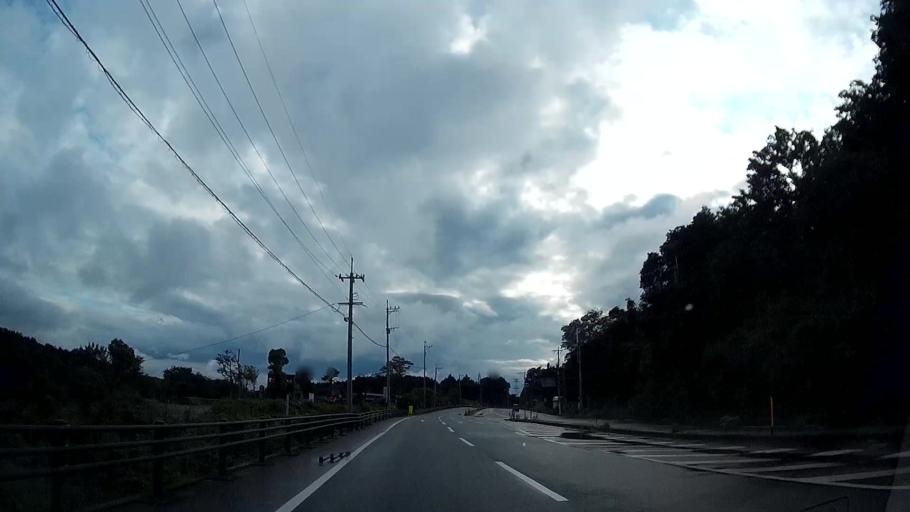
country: JP
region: Kumamoto
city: Ozu
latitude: 32.8757
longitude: 130.9337
